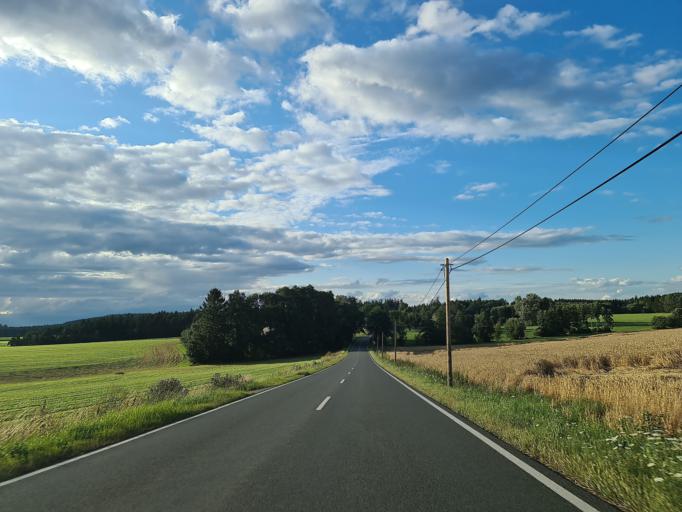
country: DE
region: Saxony
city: Pausa
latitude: 50.5956
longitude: 11.9970
